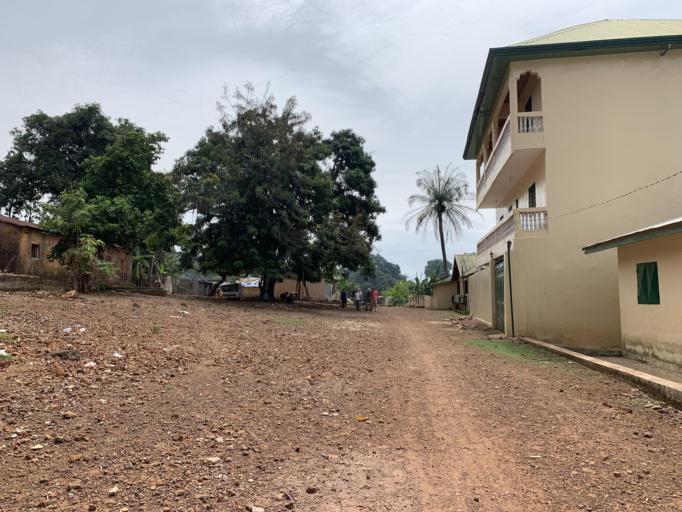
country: GN
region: Conakry
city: Camayenne
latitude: 9.5069
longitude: -13.8012
